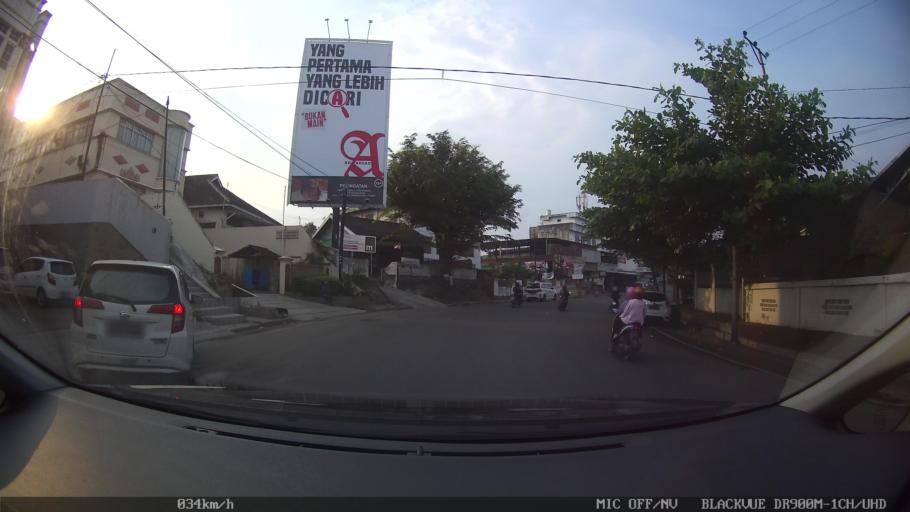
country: ID
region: Lampung
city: Bandarlampung
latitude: -5.4420
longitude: 105.2653
